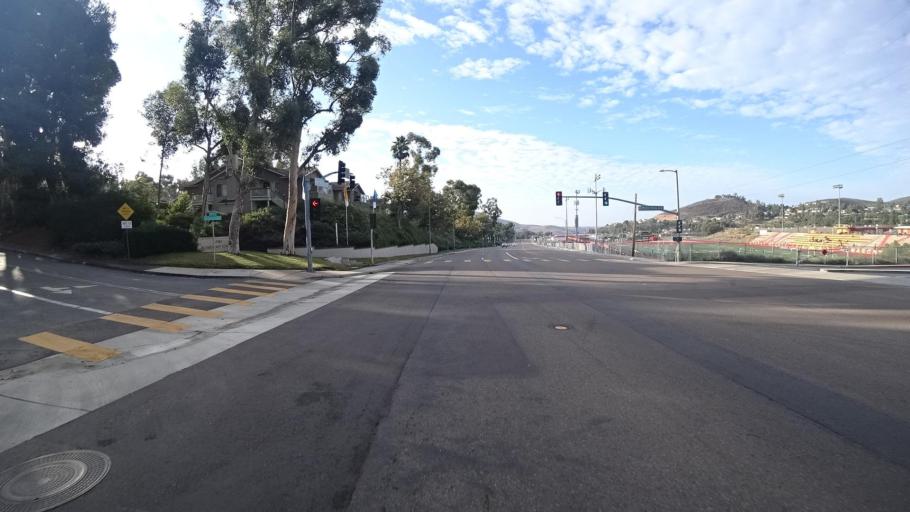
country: US
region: California
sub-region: San Diego County
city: Casa de Oro-Mount Helix
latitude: 32.7367
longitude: -116.9716
